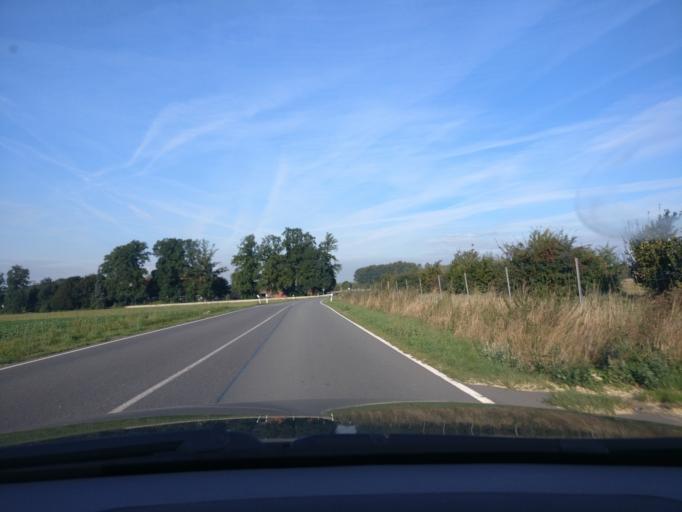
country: DE
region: Lower Saxony
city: Melle
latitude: 52.1996
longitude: 8.3026
